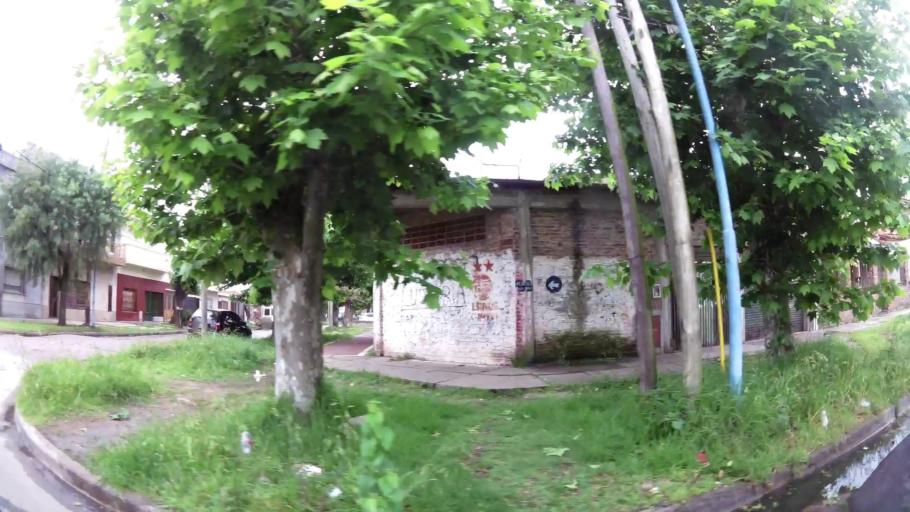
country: AR
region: Buenos Aires
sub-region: Partido de Lanus
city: Lanus
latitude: -34.7210
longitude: -58.3739
